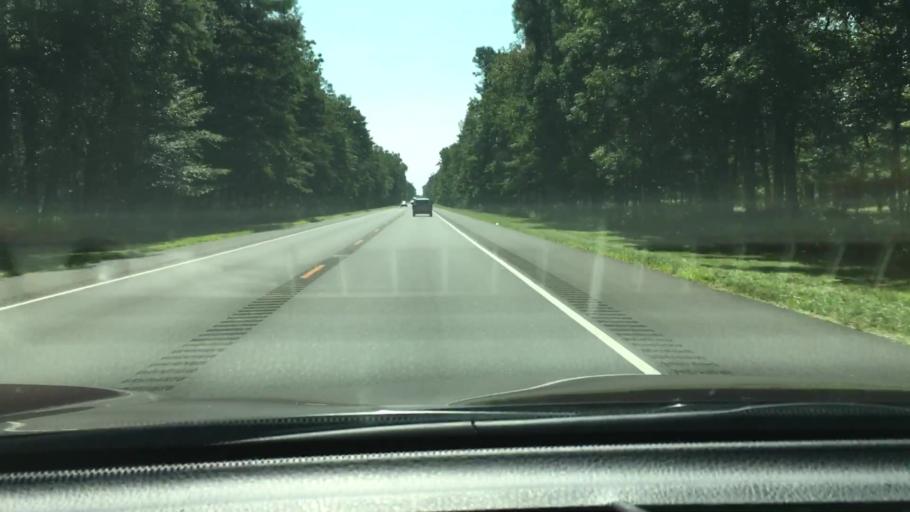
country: US
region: New Jersey
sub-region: Cape May County
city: Woodbine
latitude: 39.3407
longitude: -74.8928
